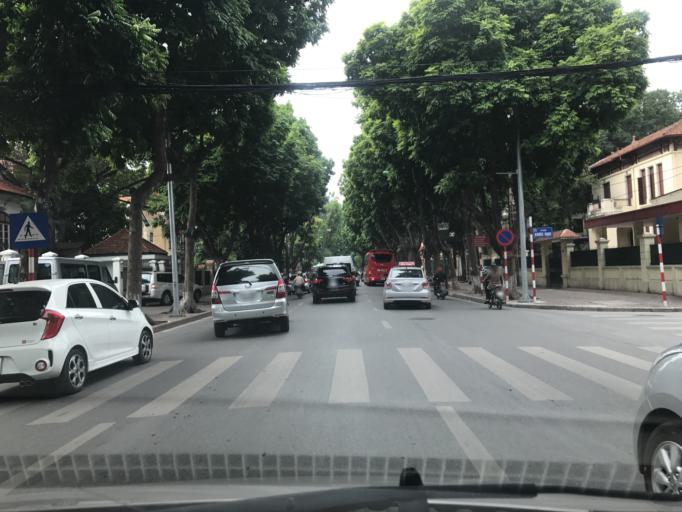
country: VN
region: Ha Noi
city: Hanoi
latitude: 21.0314
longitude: 105.8373
